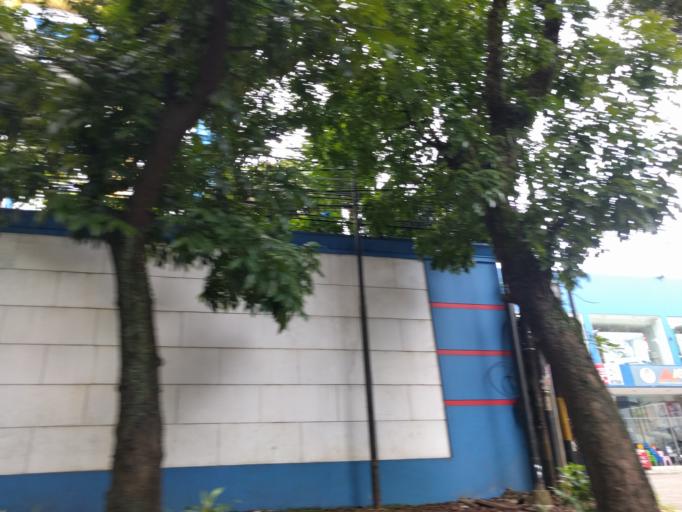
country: ID
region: West Java
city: Bogor
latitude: -6.6146
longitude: 106.8141
